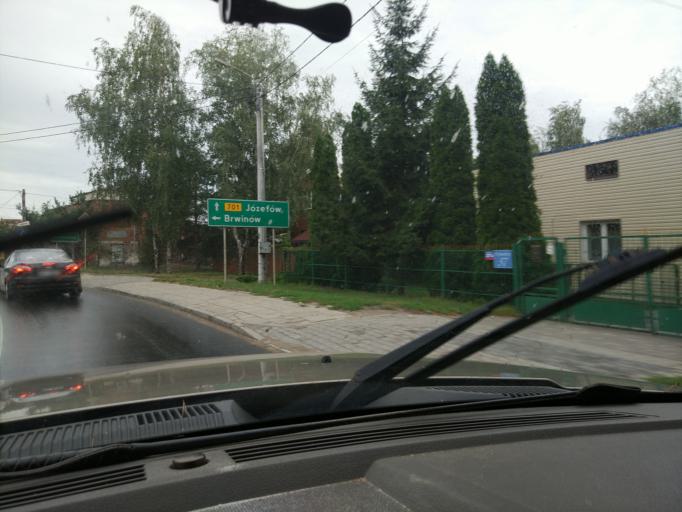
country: PL
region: Masovian Voivodeship
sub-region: Powiat warszawski zachodni
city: Ozarow Mazowiecki
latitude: 52.1902
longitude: 20.7551
